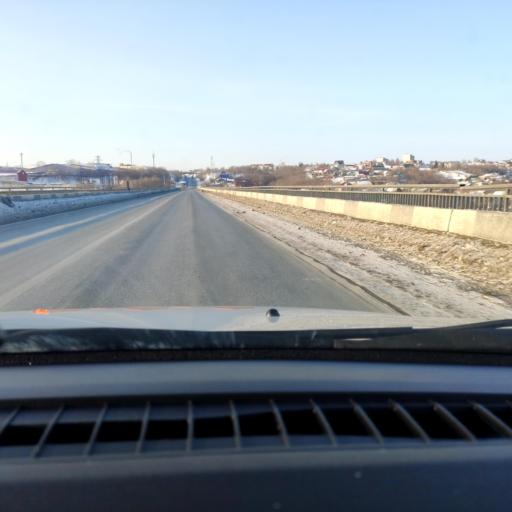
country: RU
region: Samara
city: Smyshlyayevka
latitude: 53.2336
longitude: 50.4882
